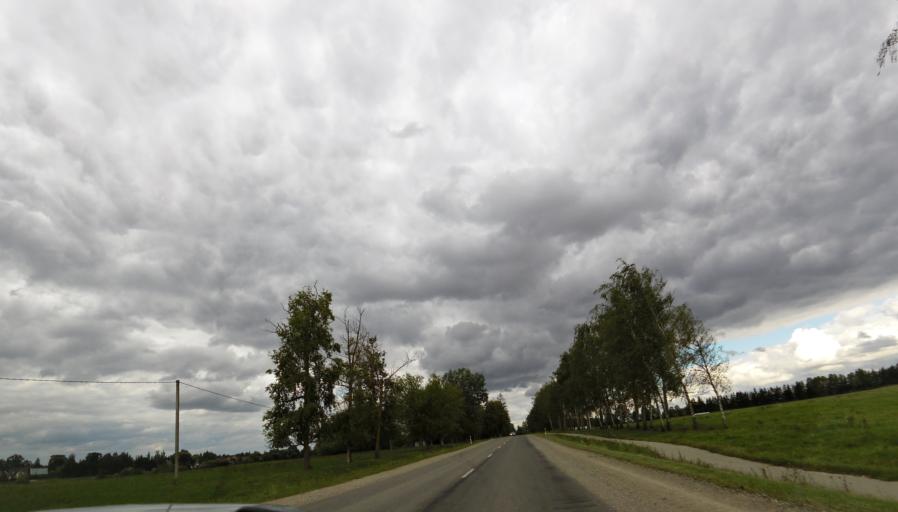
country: LT
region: Panevezys
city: Pasvalys
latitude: 56.0724
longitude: 24.3816
